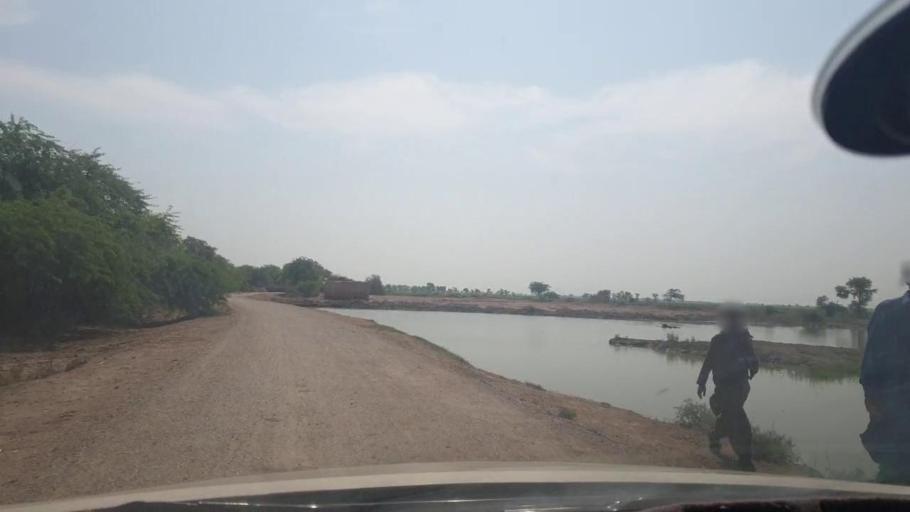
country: PK
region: Sindh
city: Jacobabad
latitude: 28.2735
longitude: 68.5261
